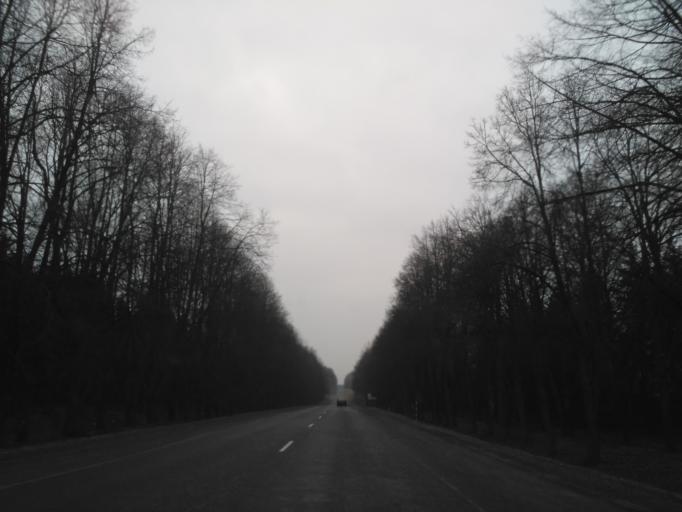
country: BY
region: Minsk
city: Snow
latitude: 53.2461
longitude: 26.2637
